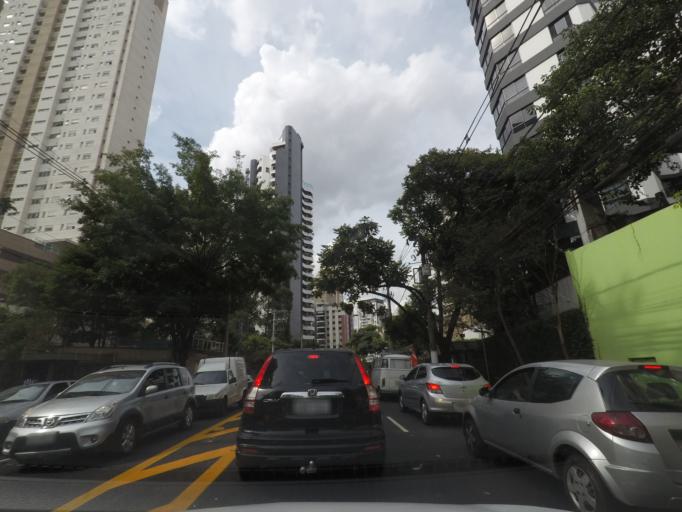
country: BR
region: Sao Paulo
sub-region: Taboao Da Serra
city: Taboao da Serra
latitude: -23.6340
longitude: -46.7325
